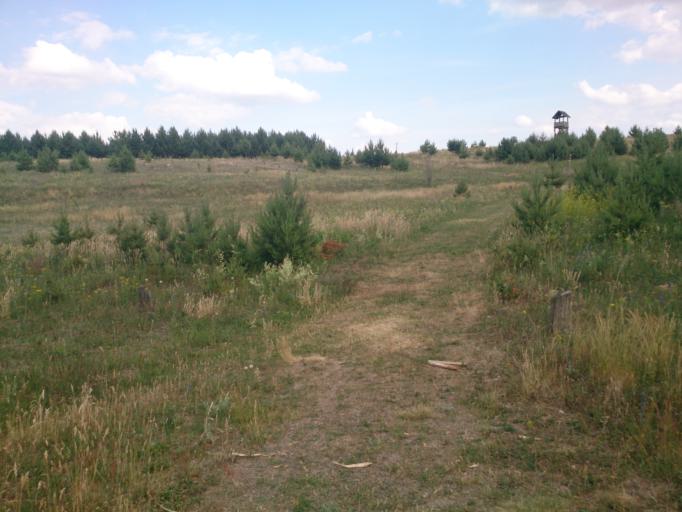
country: DE
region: Mecklenburg-Vorpommern
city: Plau am See
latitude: 53.4273
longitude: 12.3143
